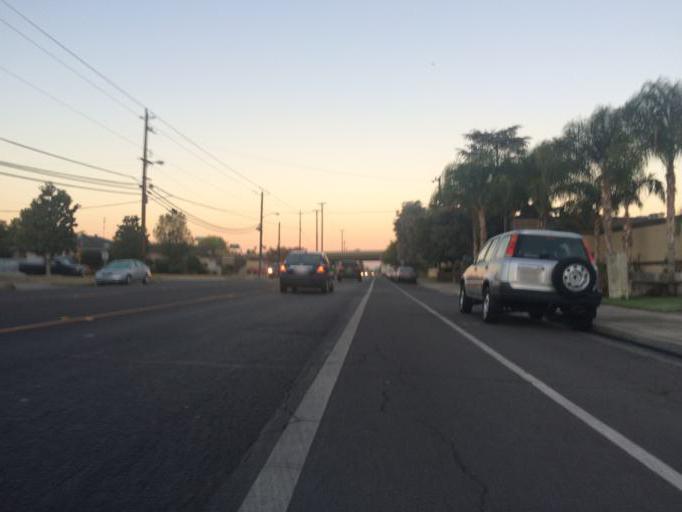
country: US
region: California
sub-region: Fresno County
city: Tarpey Village
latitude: 36.8013
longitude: -119.7376
